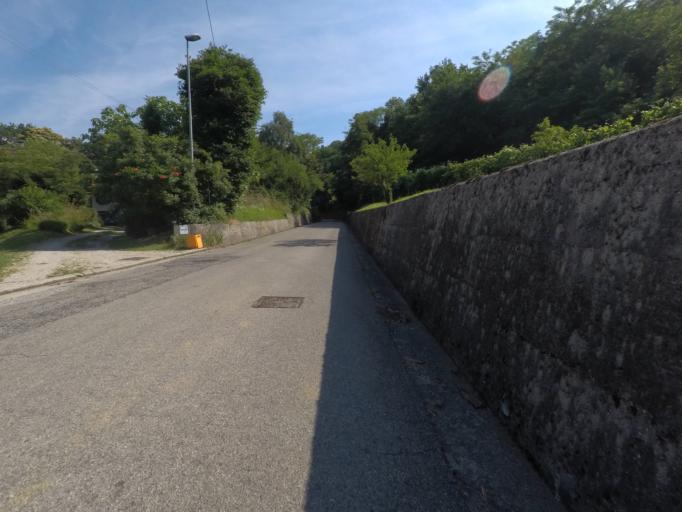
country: IT
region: Friuli Venezia Giulia
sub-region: Provincia di Udine
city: Nimis
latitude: 46.2070
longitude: 13.2747
